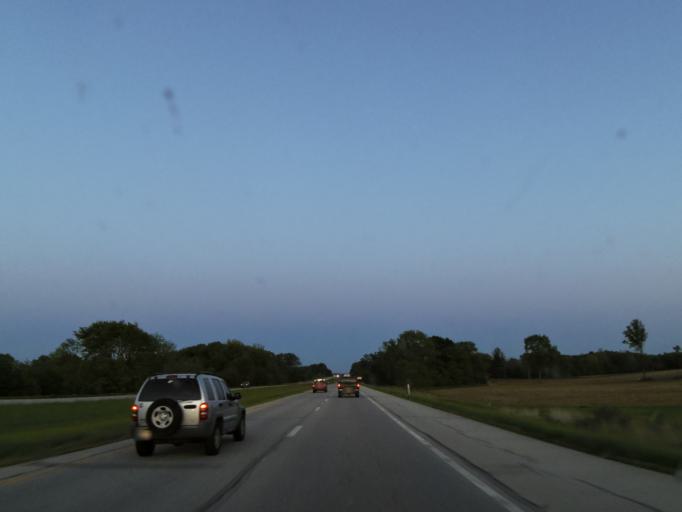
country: US
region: Indiana
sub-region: Hendricks County
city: Pittsboro
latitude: 39.9319
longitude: -86.5977
